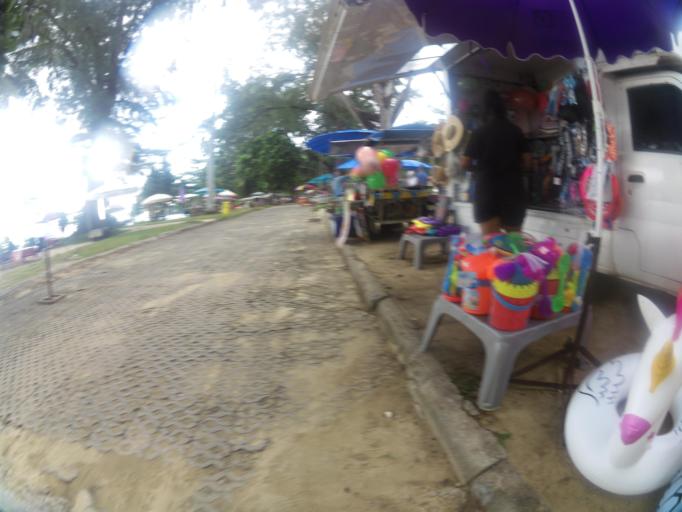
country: TH
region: Phuket
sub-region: Amphoe Kathu
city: Kathu
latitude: 7.9744
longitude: 98.2791
